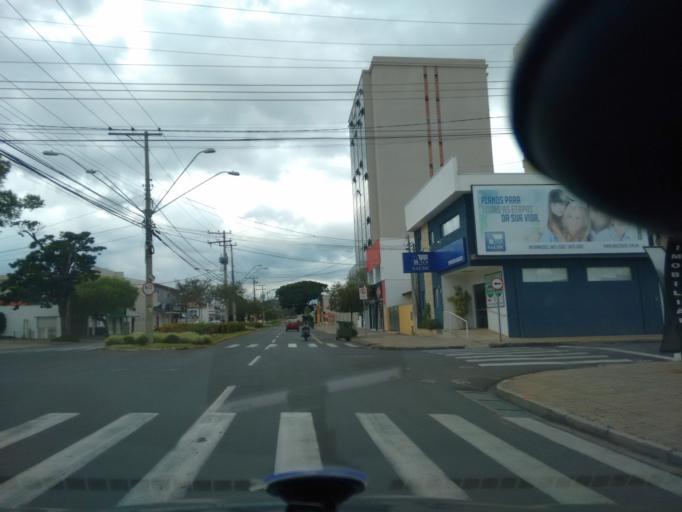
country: BR
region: Sao Paulo
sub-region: Indaiatuba
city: Indaiatuba
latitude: -23.0841
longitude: -47.2022
